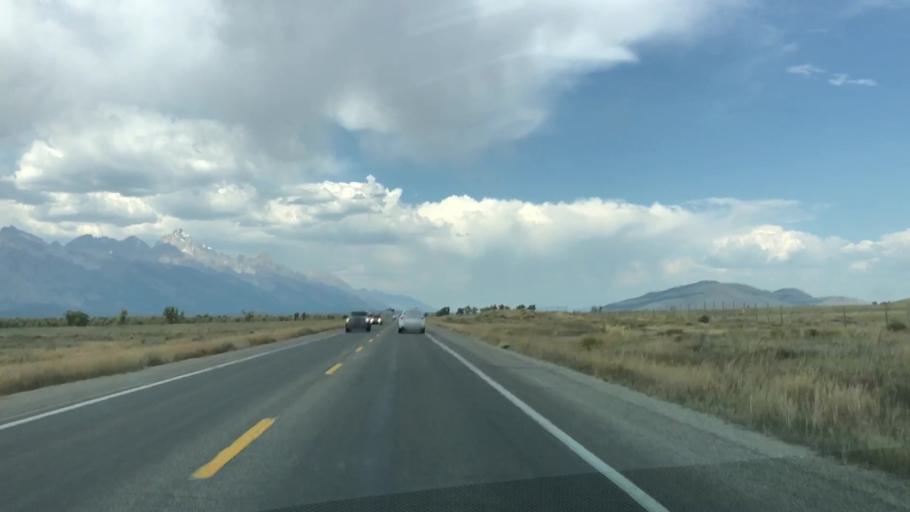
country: US
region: Wyoming
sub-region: Teton County
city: Jackson
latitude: 43.5519
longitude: -110.7337
